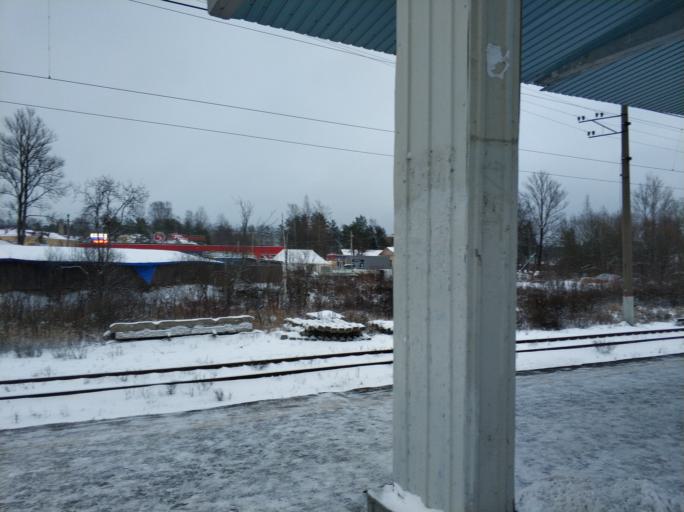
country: RU
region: Leningrad
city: Toksovo
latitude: 60.1494
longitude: 30.5090
